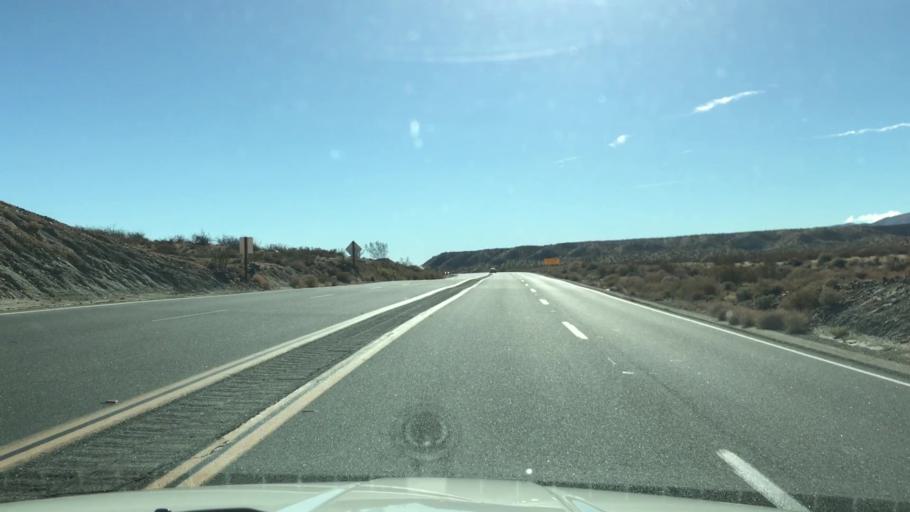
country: US
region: California
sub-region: Kern County
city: California City
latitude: 35.3419
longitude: -117.9709
